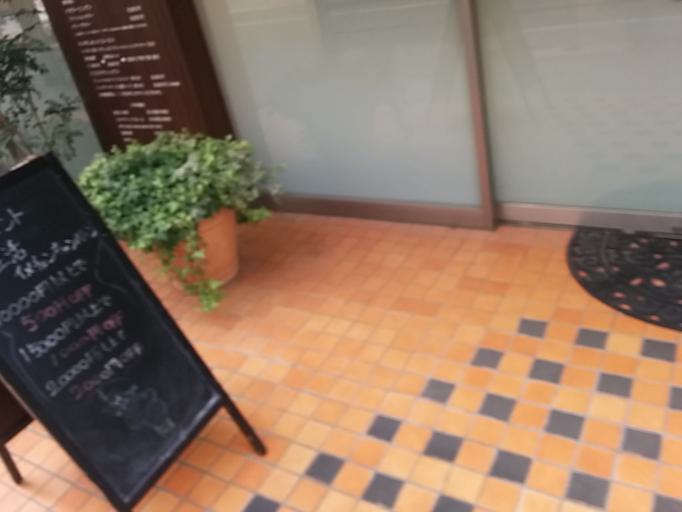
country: JP
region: Tokyo
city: Urayasu
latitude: 35.6635
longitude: 139.8588
